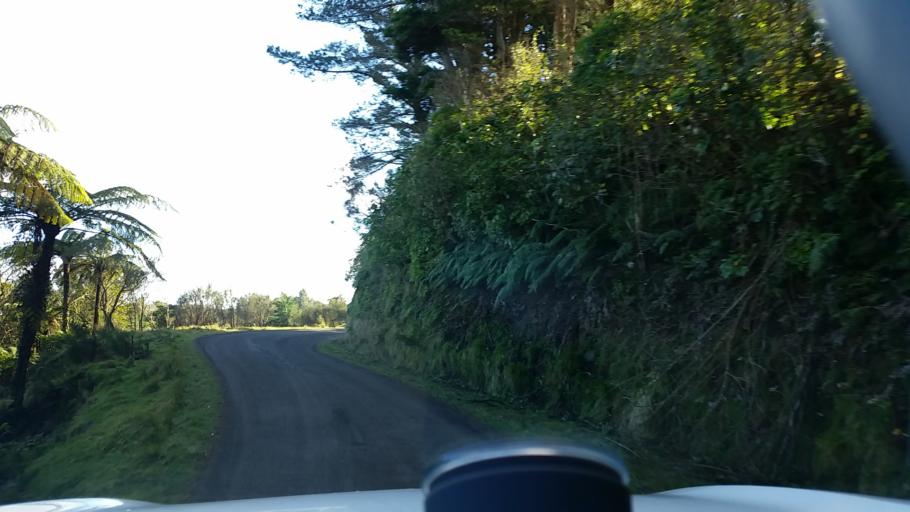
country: NZ
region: Taranaki
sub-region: South Taranaki District
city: Eltham
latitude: -39.4034
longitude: 174.5685
